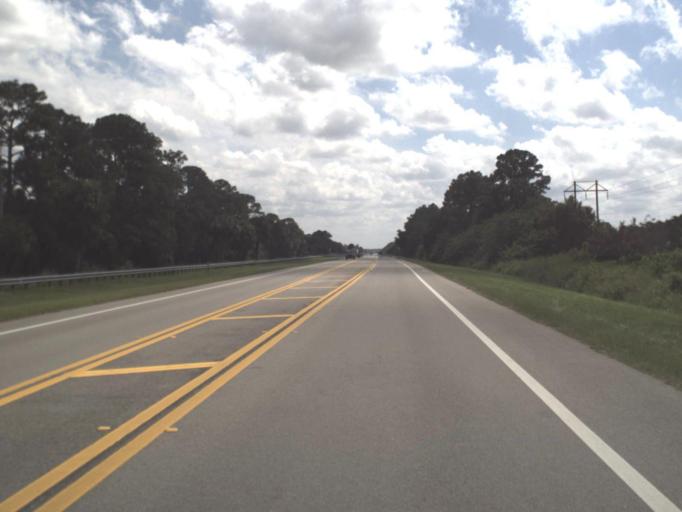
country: US
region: Florida
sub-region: Collier County
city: Immokalee
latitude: 26.3971
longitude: -81.3849
